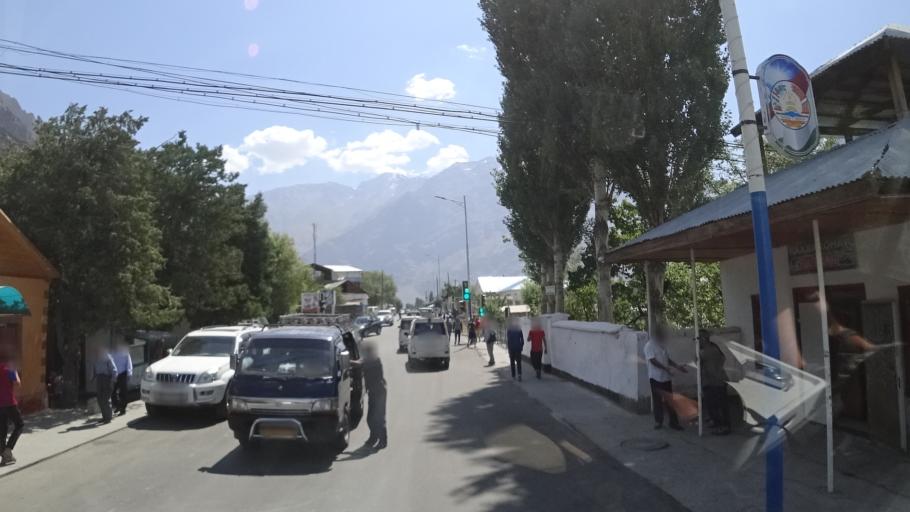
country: TJ
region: Gorno-Badakhshan
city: Rushon
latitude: 37.9472
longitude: 71.5581
